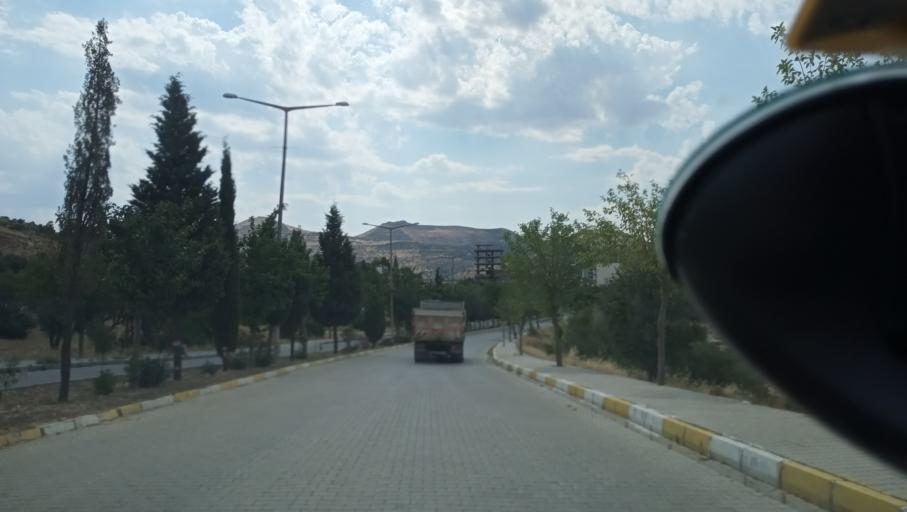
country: TR
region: Mardin
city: Kabala
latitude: 37.3421
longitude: 40.8083
